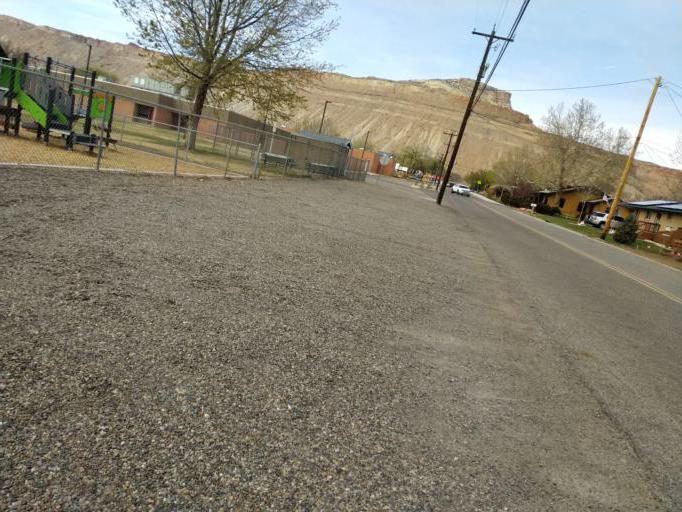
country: US
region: Colorado
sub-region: Mesa County
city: Palisade
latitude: 39.1035
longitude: -108.3528
